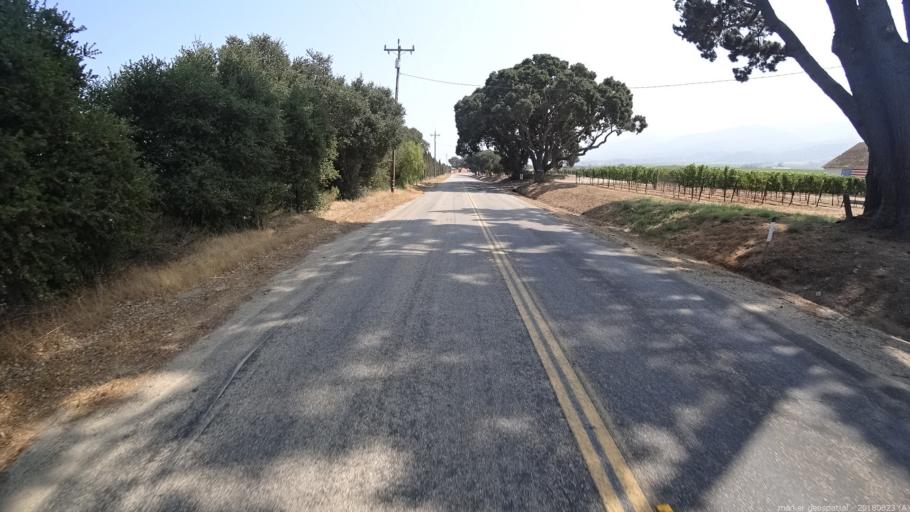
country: US
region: California
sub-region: Monterey County
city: Gonzales
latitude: 36.4464
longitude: -121.4326
